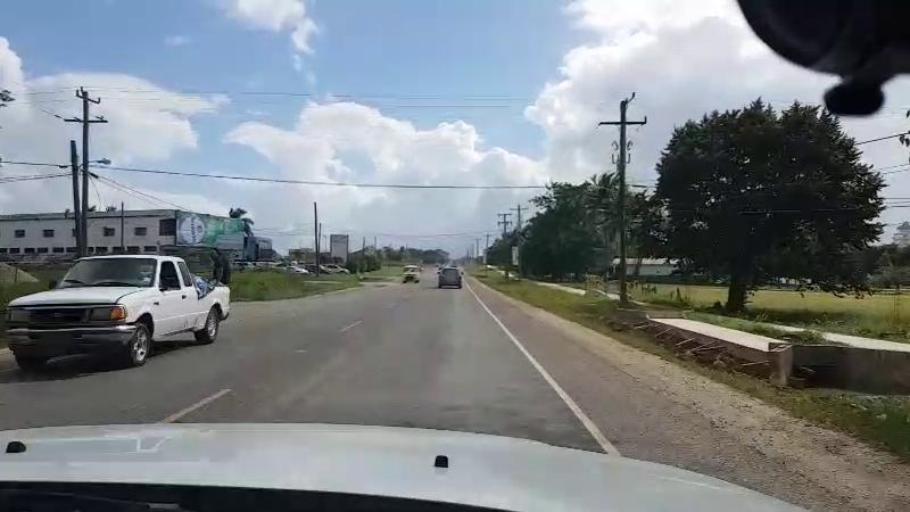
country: BZ
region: Cayo
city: Belmopan
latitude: 17.2567
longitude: -88.7863
